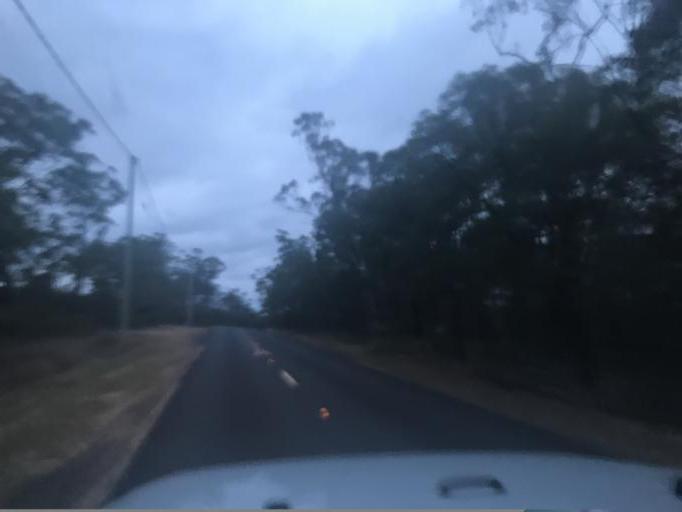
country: AU
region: New South Wales
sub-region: Hawkesbury
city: Pitt Town
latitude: -33.4682
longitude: 150.8521
